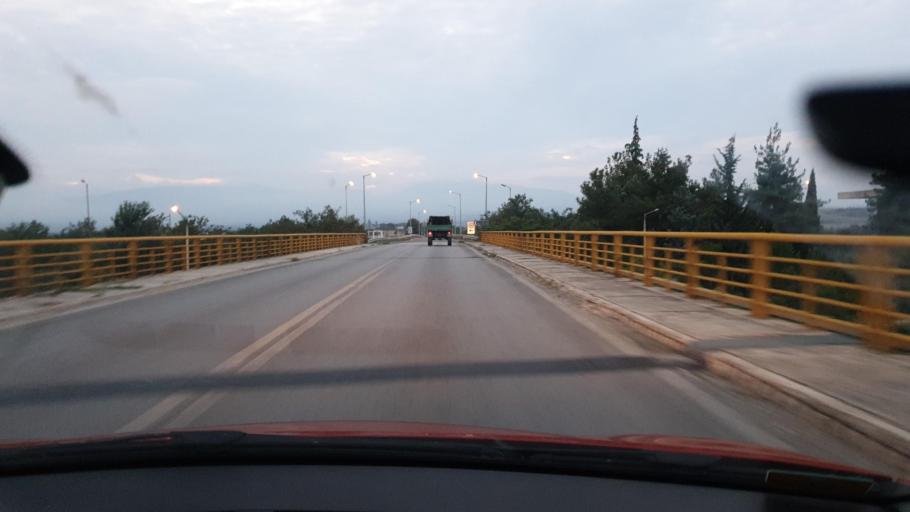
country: GR
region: Central Macedonia
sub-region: Nomos Kilkis
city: Polykastro
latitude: 40.9907
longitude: 22.6044
